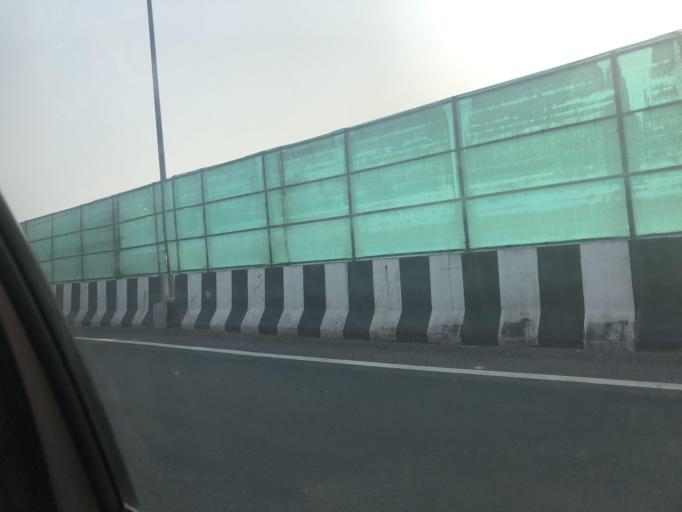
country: IN
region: NCT
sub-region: Central Delhi
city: Karol Bagh
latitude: 28.5913
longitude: 77.1589
